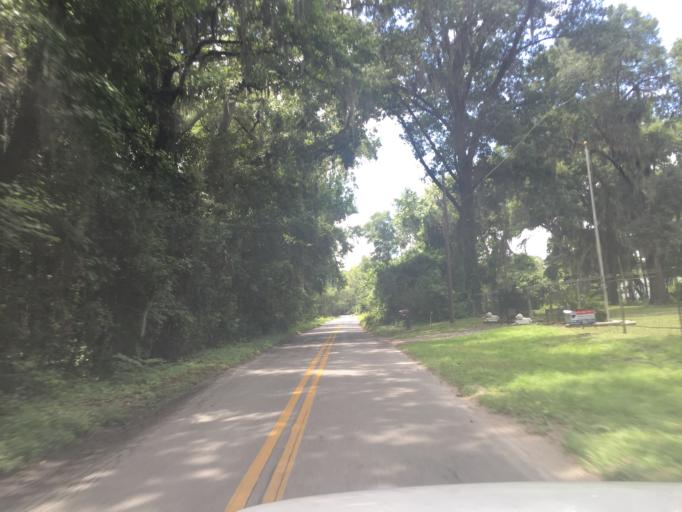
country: US
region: Georgia
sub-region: Chatham County
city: Montgomery
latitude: 31.9461
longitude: -81.1064
